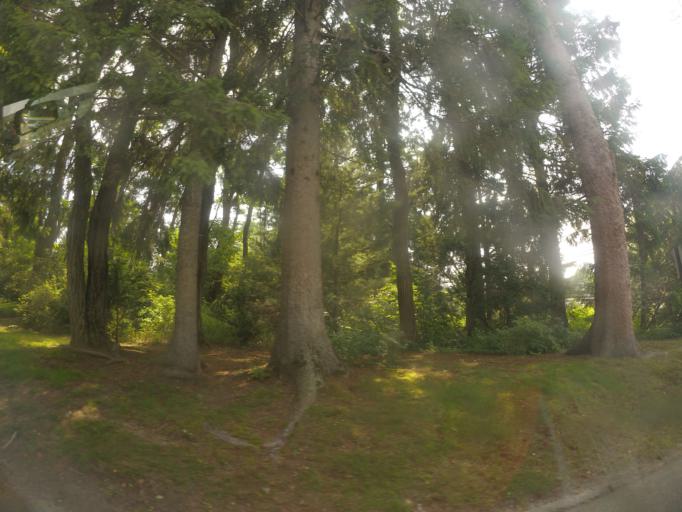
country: US
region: Maine
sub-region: Cumberland County
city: Falmouth
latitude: 43.7193
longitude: -70.2267
